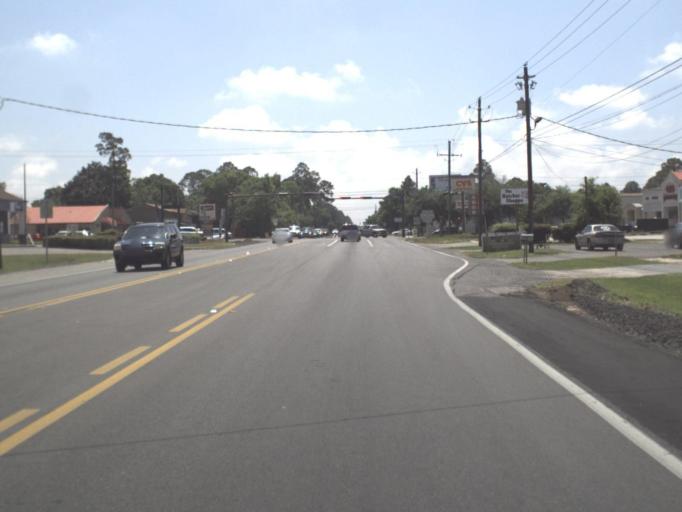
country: US
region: Florida
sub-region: Escambia County
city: Myrtle Grove
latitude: 30.4224
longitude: -87.3173
